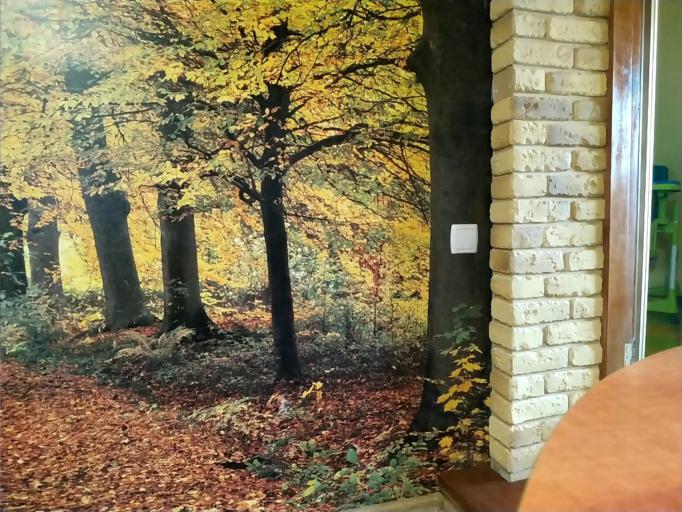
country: RU
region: Leningrad
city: Tolmachevo
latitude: 58.9484
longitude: 29.6409
